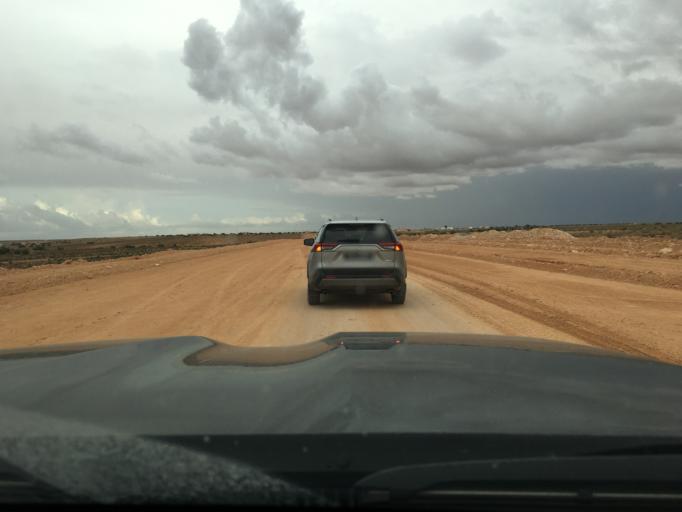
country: TN
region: Madanin
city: Medenine
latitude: 33.2847
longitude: 10.5984
